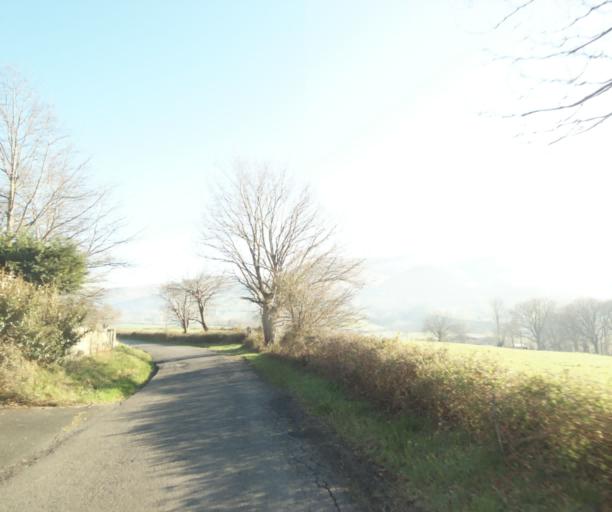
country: FR
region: Aquitaine
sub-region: Departement des Pyrenees-Atlantiques
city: Urrugne
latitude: 43.3491
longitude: -1.7072
